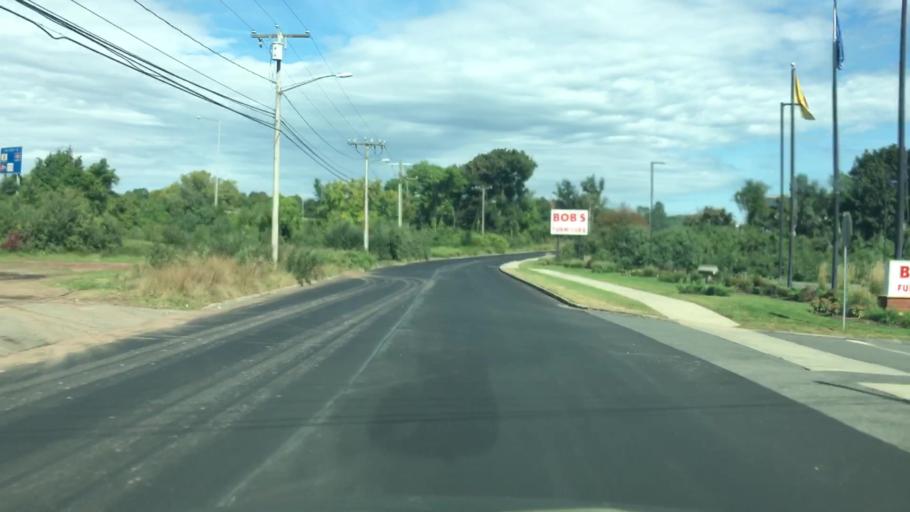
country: US
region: Connecticut
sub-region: Hartford County
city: Manchester
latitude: 41.8087
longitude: -72.5255
